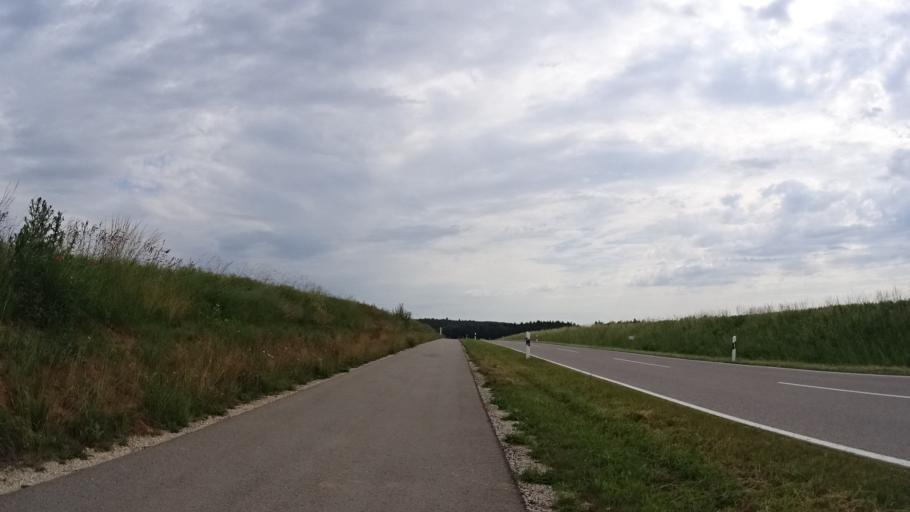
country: DE
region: Bavaria
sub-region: Upper Bavaria
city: Stammham
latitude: 48.8645
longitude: 11.4745
